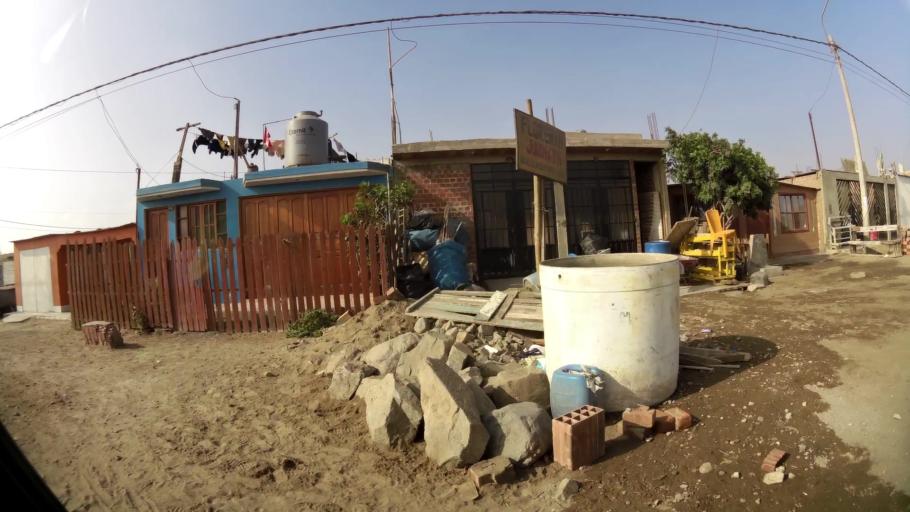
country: PE
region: Lima
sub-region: Lima
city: Santa Rosa
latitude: -11.7652
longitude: -77.1672
